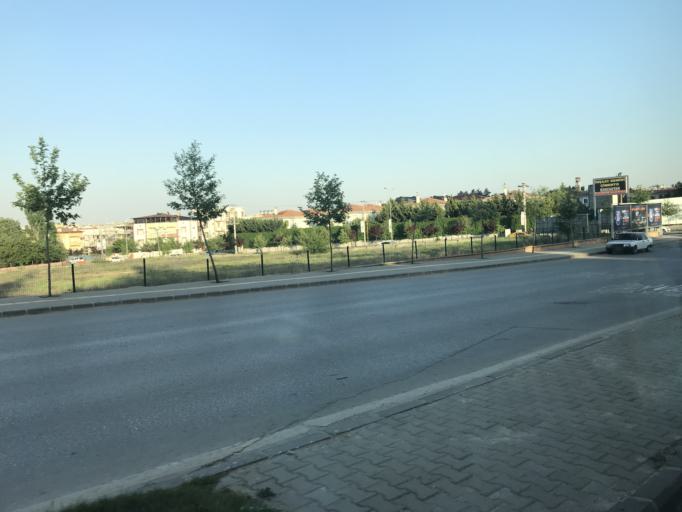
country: TR
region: Gaziantep
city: Sahinbey
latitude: 37.0546
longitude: 37.3209
